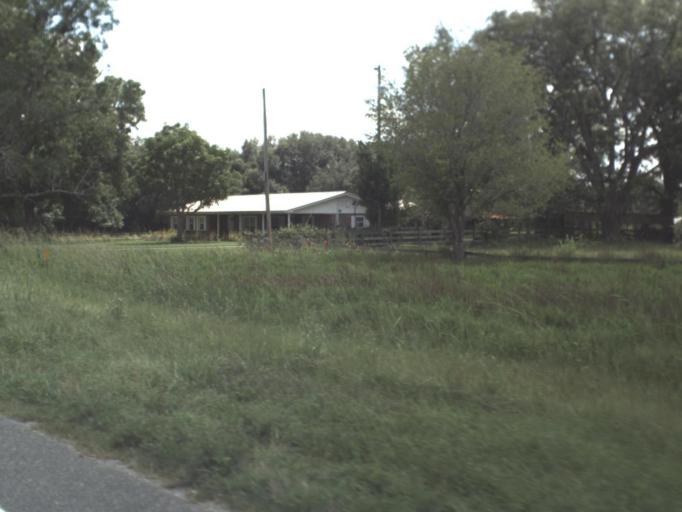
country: US
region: Florida
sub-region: Columbia County
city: Watertown
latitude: 30.0180
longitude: -82.5975
